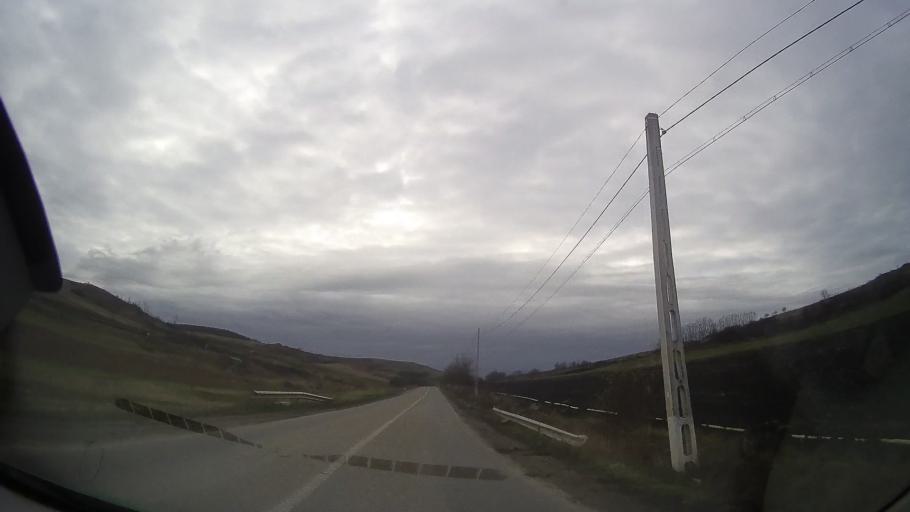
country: RO
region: Bistrita-Nasaud
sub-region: Comuna Budesti
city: Budesti
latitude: 46.8555
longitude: 24.2434
